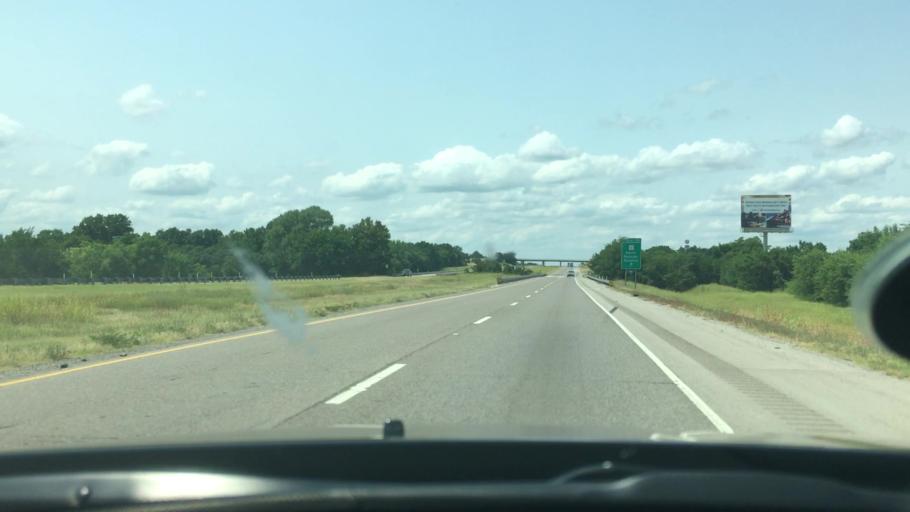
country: US
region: Oklahoma
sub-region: Murray County
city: Davis
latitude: 34.4988
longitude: -97.1689
